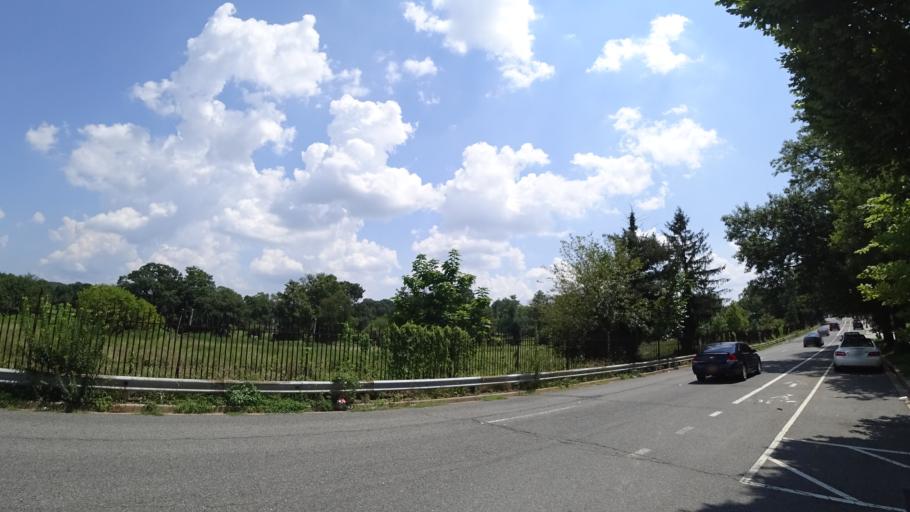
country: US
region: Maryland
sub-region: Prince George's County
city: Chillum
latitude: 38.9358
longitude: -77.0193
